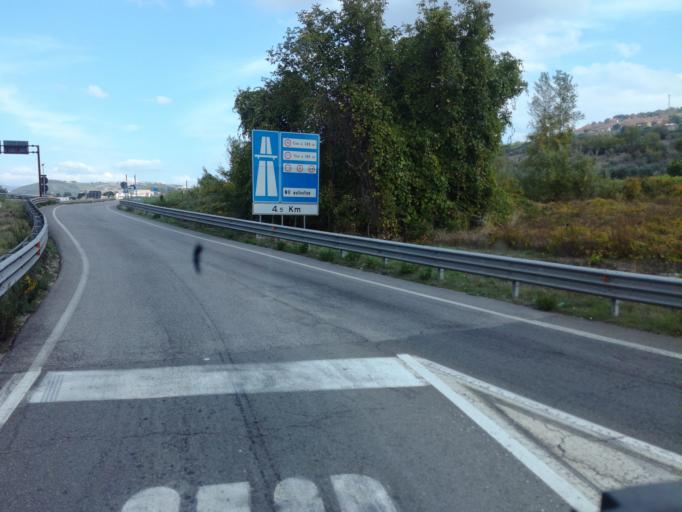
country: IT
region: Campania
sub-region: Provincia di Benevento
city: Ponte
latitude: 41.1892
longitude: 14.7411
